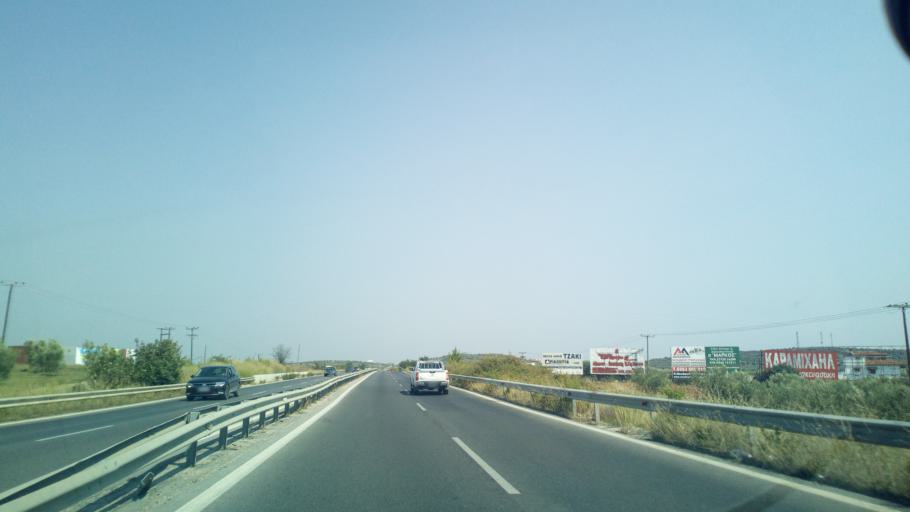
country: GR
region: Central Macedonia
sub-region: Nomos Chalkidikis
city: Nea Moudhania
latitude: 40.2628
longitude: 23.2565
